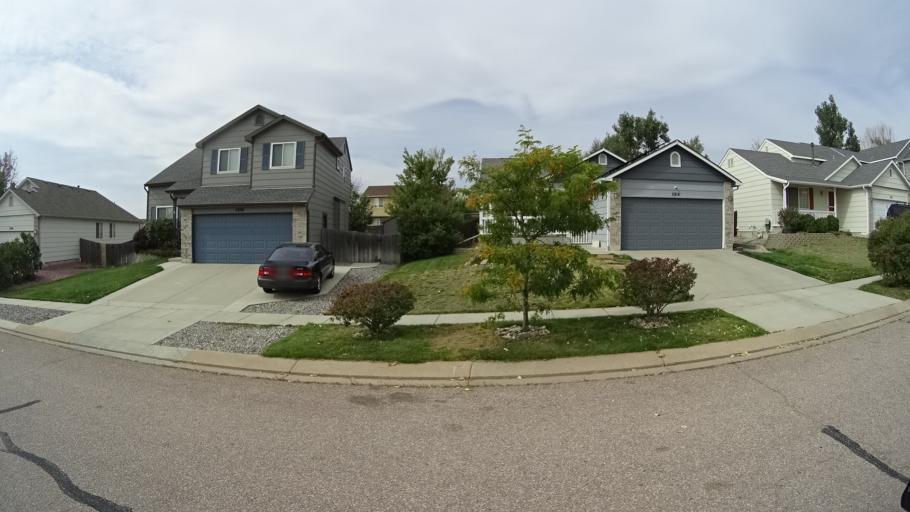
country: US
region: Colorado
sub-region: El Paso County
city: Cimarron Hills
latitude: 38.9161
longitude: -104.7133
